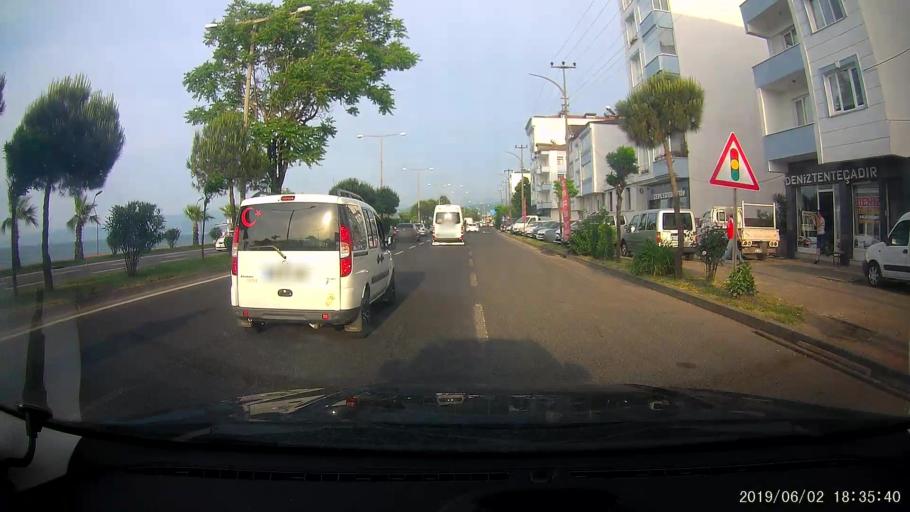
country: TR
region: Ordu
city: Fatsa
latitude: 41.0259
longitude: 37.5190
